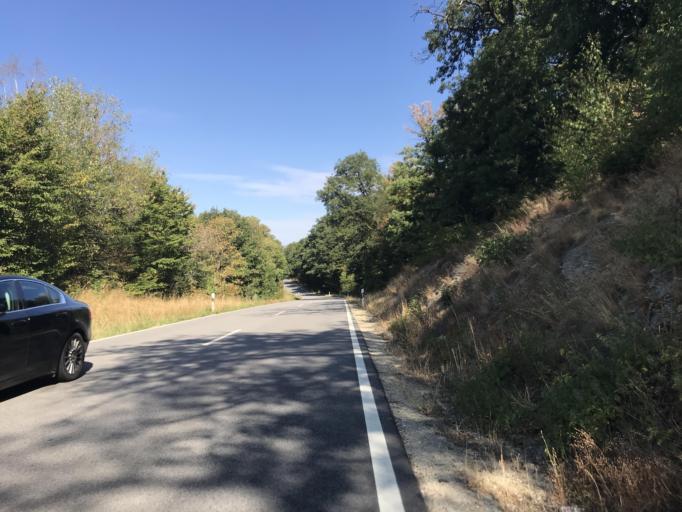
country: DE
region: Hesse
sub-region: Regierungsbezirk Darmstadt
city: Rudesheim am Rhein
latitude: 50.0486
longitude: 7.9253
